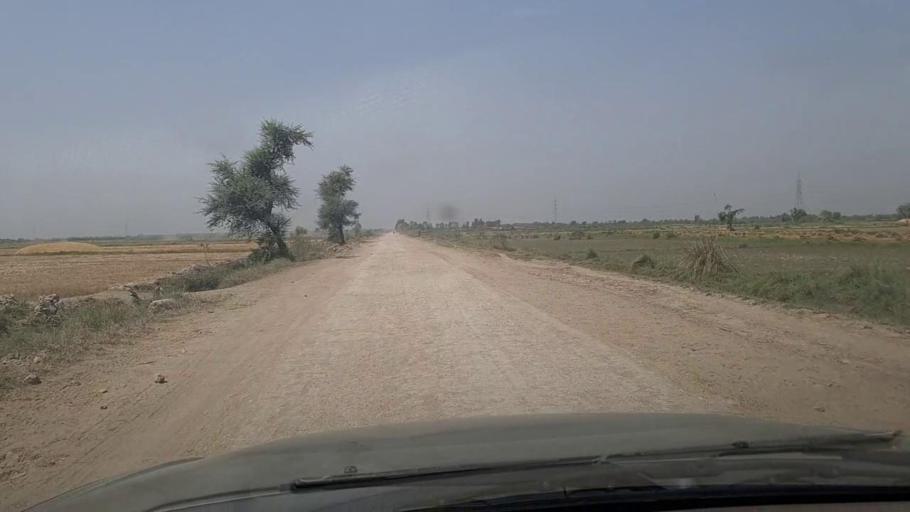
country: PK
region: Sindh
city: Adilpur
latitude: 27.9397
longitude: 69.3057
